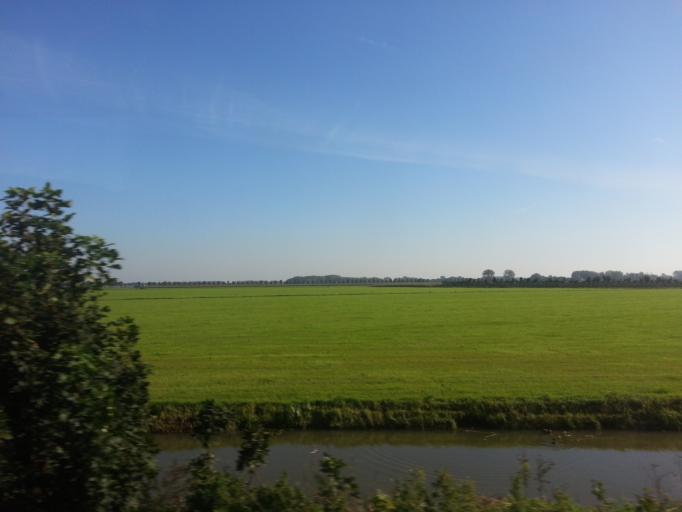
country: NL
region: Gelderland
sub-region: Gemeente Geldermalsen
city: Geldermalsen
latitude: 51.9010
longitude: 5.2628
